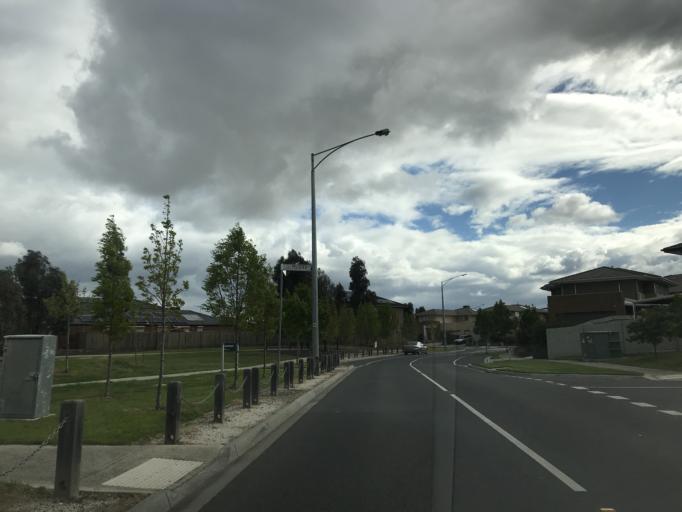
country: AU
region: Victoria
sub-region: Brimbank
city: Sunshine West
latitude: -37.7938
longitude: 144.7968
